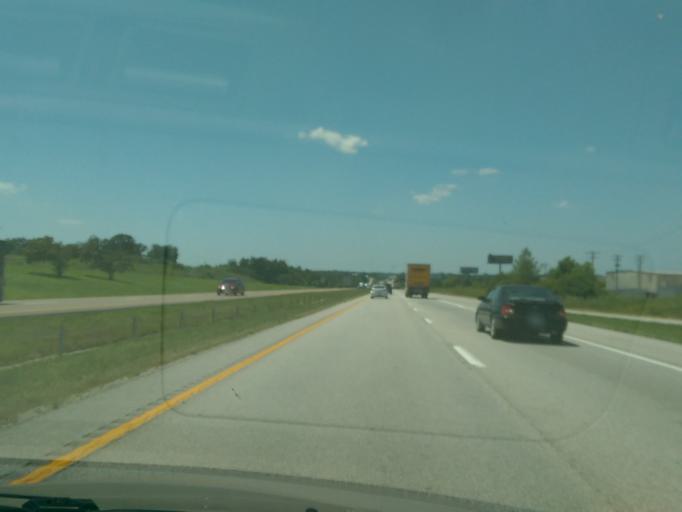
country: US
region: Missouri
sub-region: Cooper County
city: Boonville
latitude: 38.9358
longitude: -92.7783
